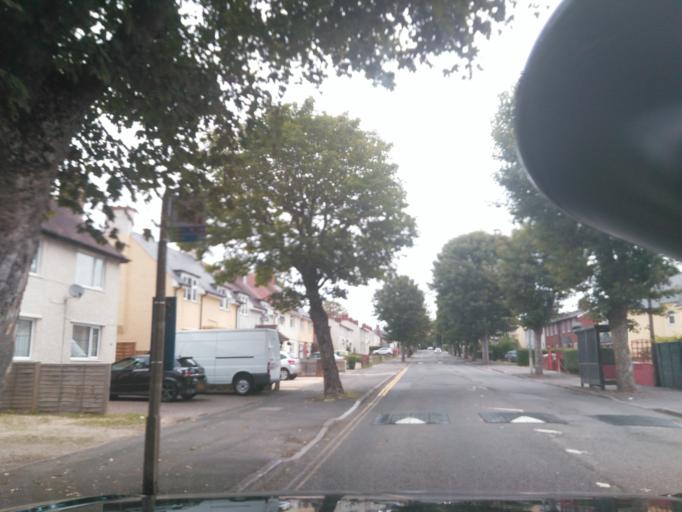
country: GB
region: England
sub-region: Borough of Swindon
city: Swindon
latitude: 51.5775
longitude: -1.7851
